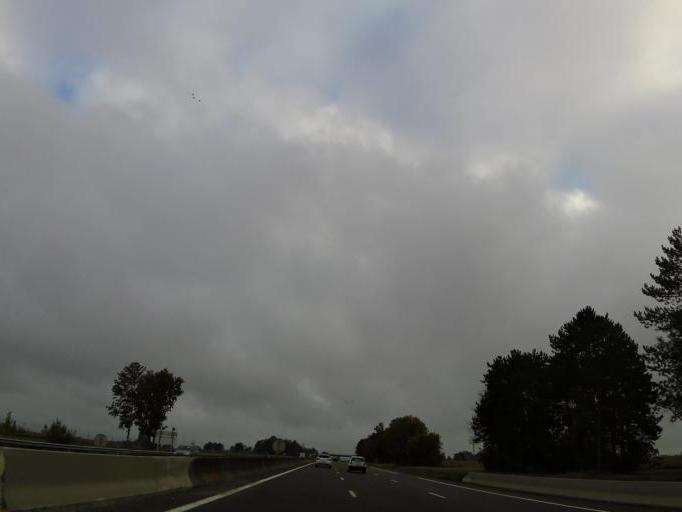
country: FR
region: Ile-de-France
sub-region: Departement de Seine-et-Marne
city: Bailly-Romainvilliers
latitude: 48.8562
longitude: 2.8404
